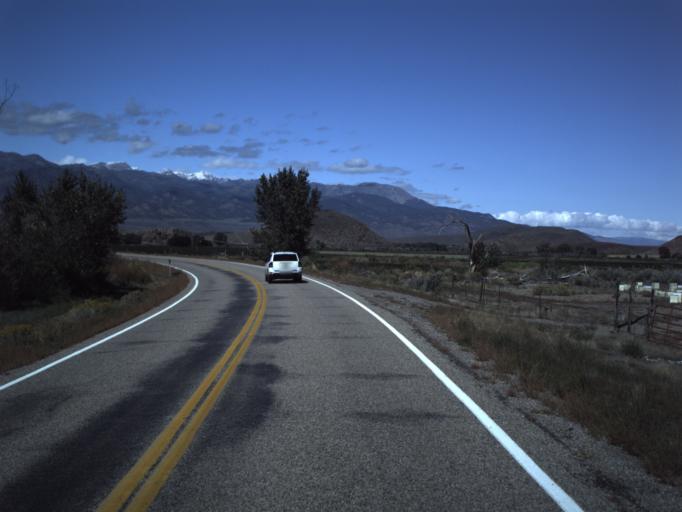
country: US
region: Utah
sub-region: Piute County
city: Junction
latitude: 38.2069
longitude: -112.1811
